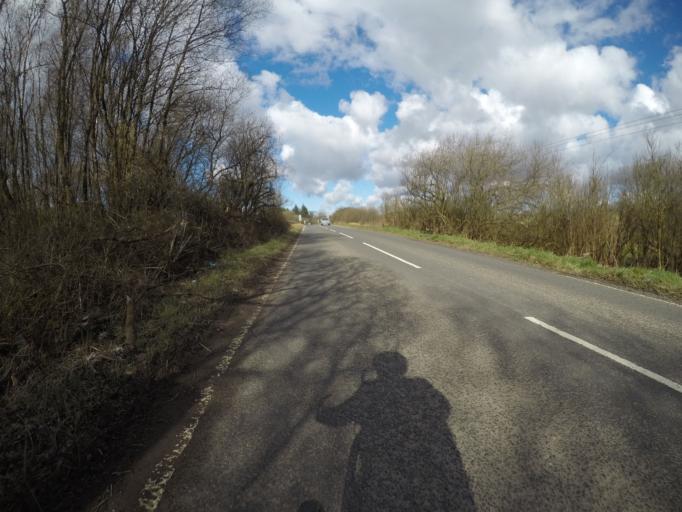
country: GB
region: Scotland
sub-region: North Ayrshire
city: Beith
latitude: 55.7317
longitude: -4.6088
